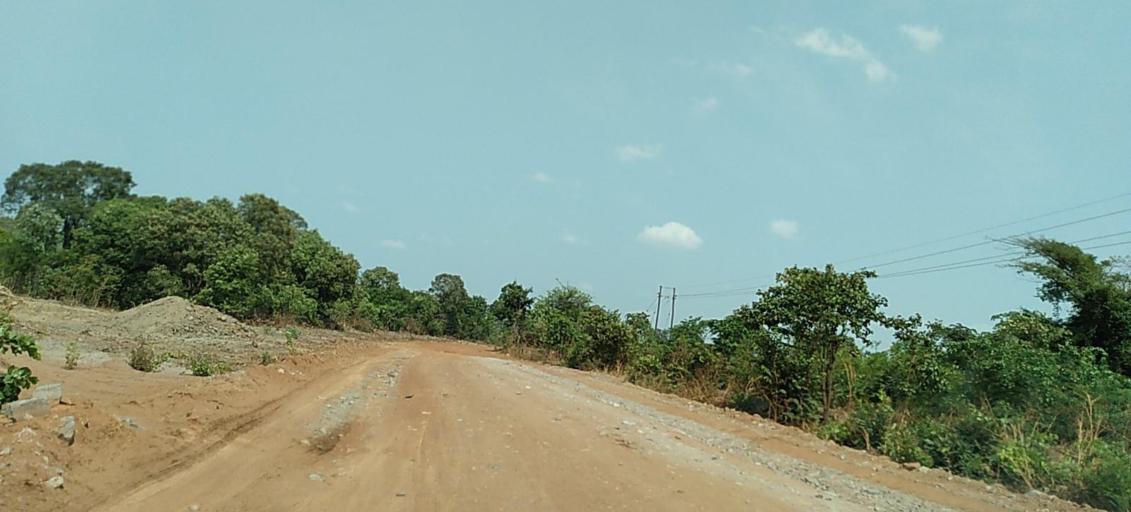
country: ZM
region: Copperbelt
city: Luanshya
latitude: -13.0932
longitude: 28.3099
